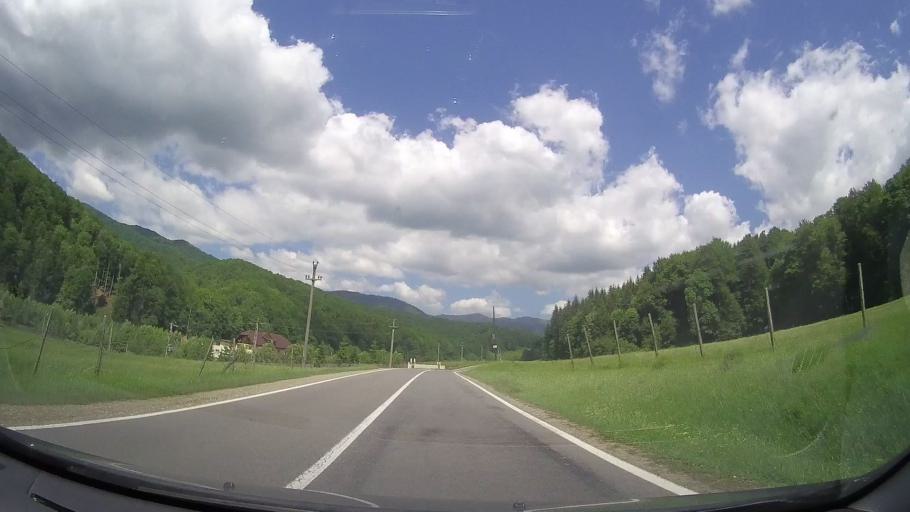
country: RO
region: Prahova
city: Maneciu
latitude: 45.4284
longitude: 25.9398
